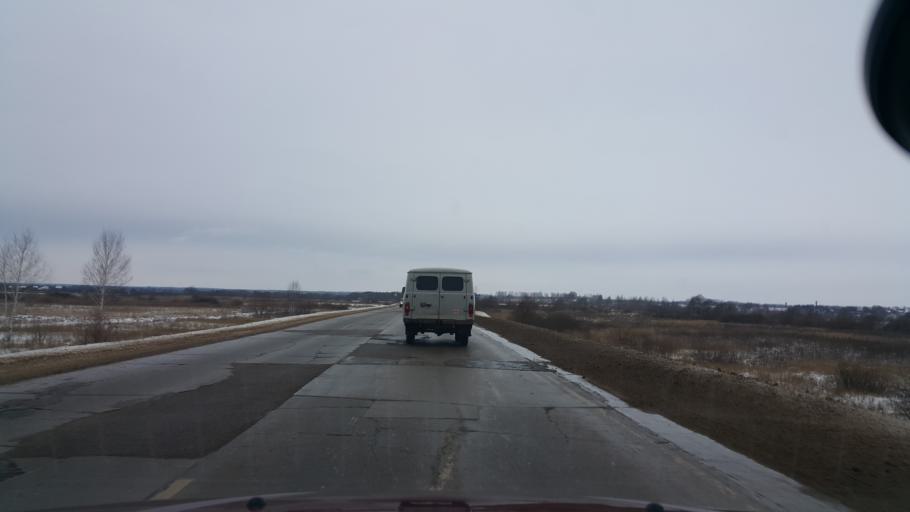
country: RU
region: Tambov
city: Bokino
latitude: 52.6199
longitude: 41.4793
